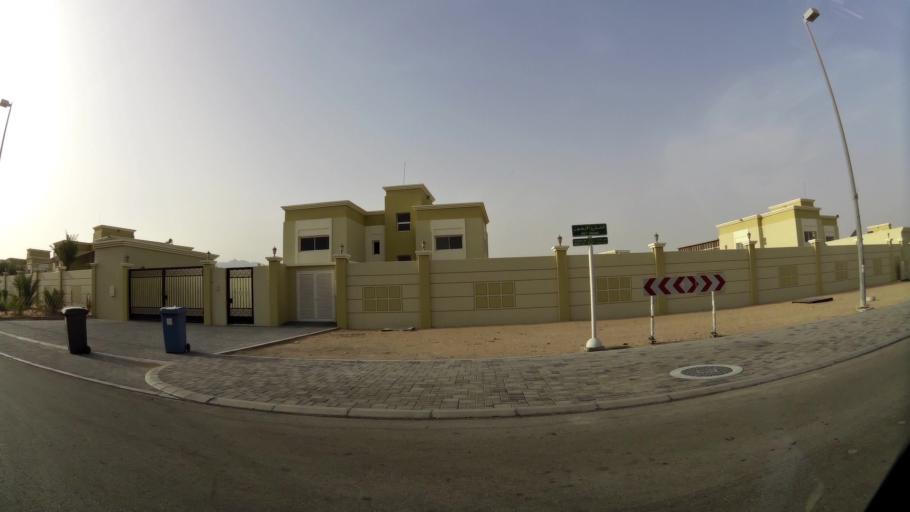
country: AE
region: Abu Dhabi
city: Al Ain
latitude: 24.1163
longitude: 55.7069
